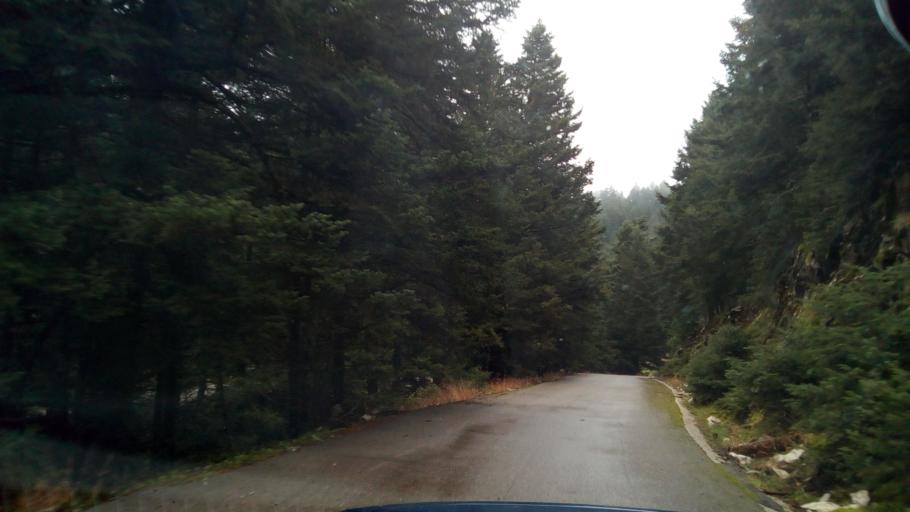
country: GR
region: West Greece
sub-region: Nomos Aitolias kai Akarnanias
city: Nafpaktos
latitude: 38.5364
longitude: 21.8562
